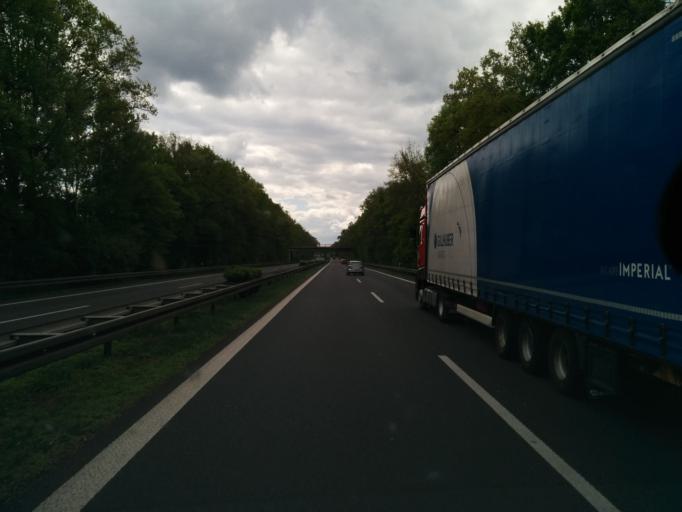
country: DE
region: Brandenburg
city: Gross Kreutz
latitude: 52.3632
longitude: 12.8153
